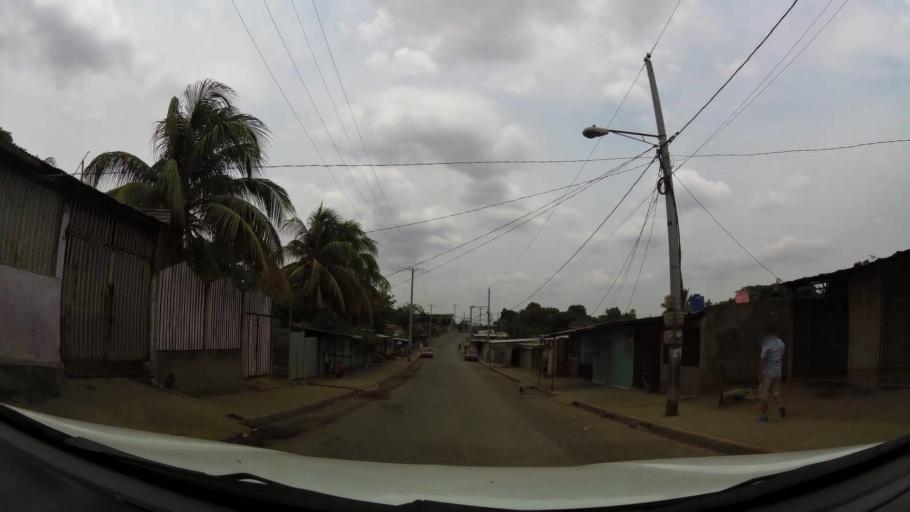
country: NI
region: Managua
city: Managua
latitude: 12.1097
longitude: -86.2220
